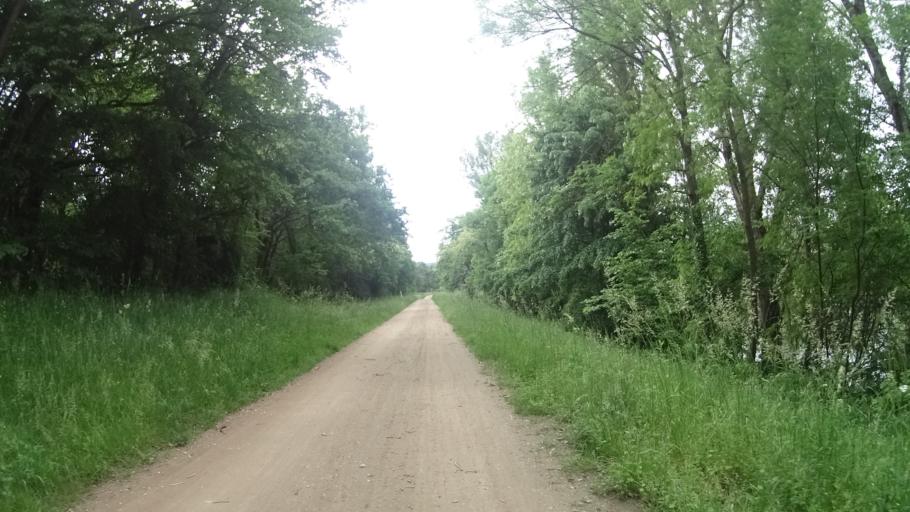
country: FR
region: Alsace
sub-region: Departement du Haut-Rhin
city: Kembs
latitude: 47.6915
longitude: 7.5166
